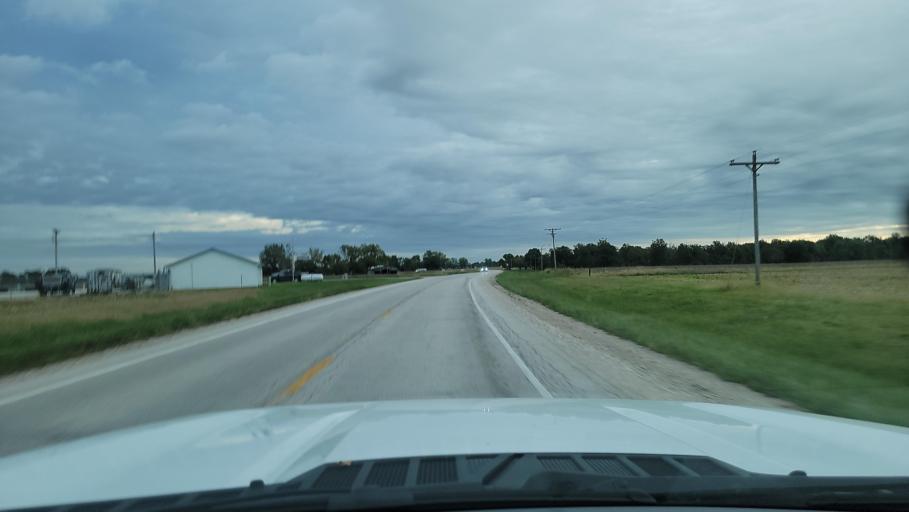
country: US
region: Illinois
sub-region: Schuyler County
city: Rushville
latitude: 40.0796
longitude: -90.6137
